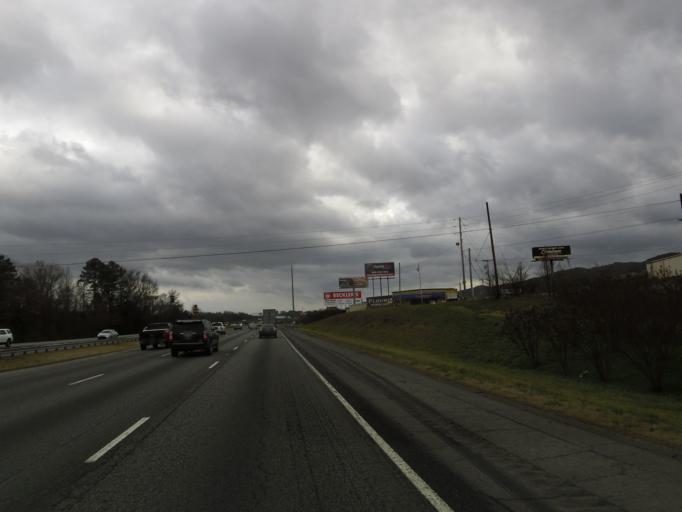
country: US
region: Georgia
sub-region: Whitfield County
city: Dalton
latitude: 34.6931
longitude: -85.0037
